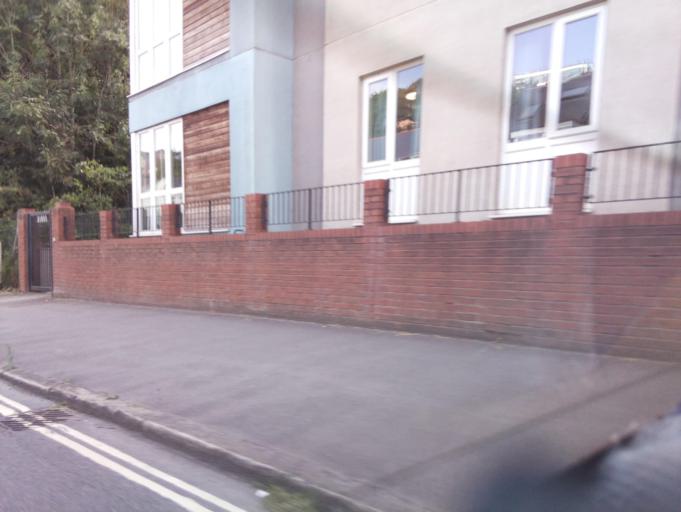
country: GB
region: England
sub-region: Devon
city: Exeter
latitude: 50.7267
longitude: -3.5421
